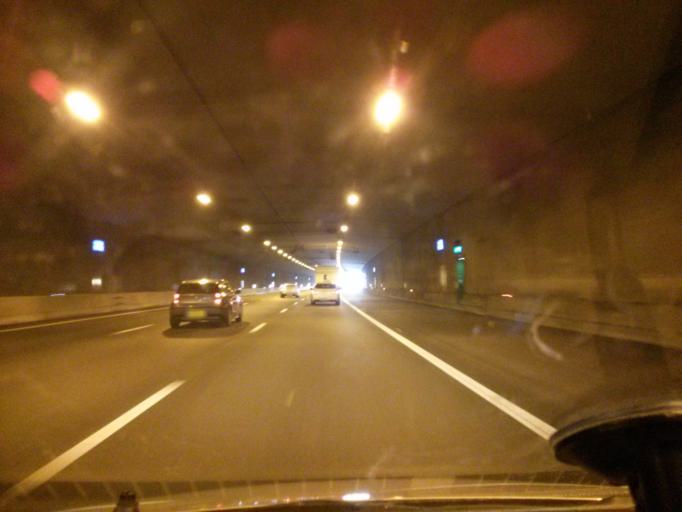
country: NL
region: Utrecht
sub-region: Stichtse Vecht
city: Maarssen
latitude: 52.0989
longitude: 5.0672
